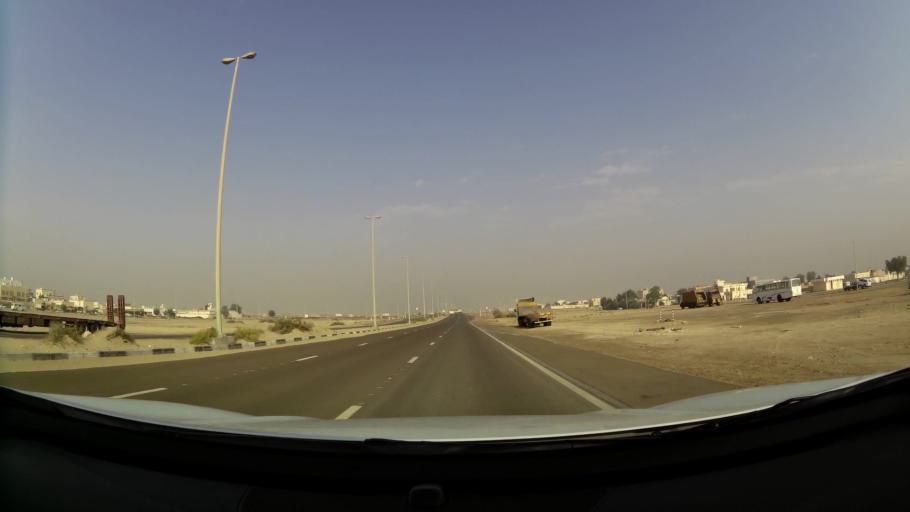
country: AE
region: Abu Dhabi
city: Abu Dhabi
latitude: 24.2724
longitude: 54.6488
